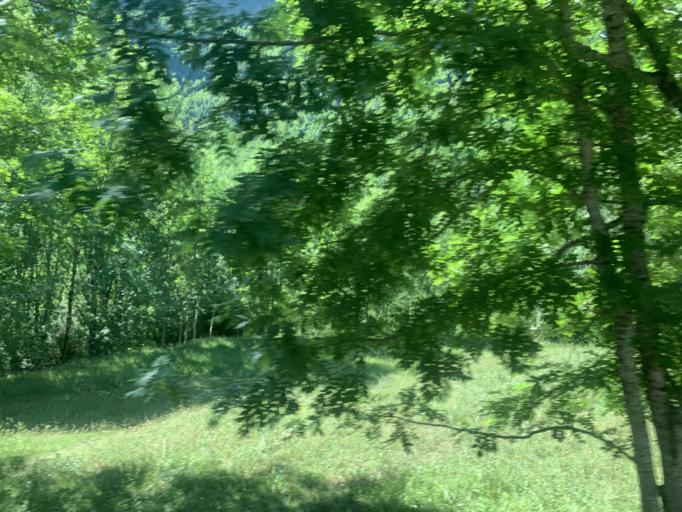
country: ES
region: Aragon
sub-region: Provincia de Huesca
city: Broto
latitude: 42.6510
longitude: -0.0681
